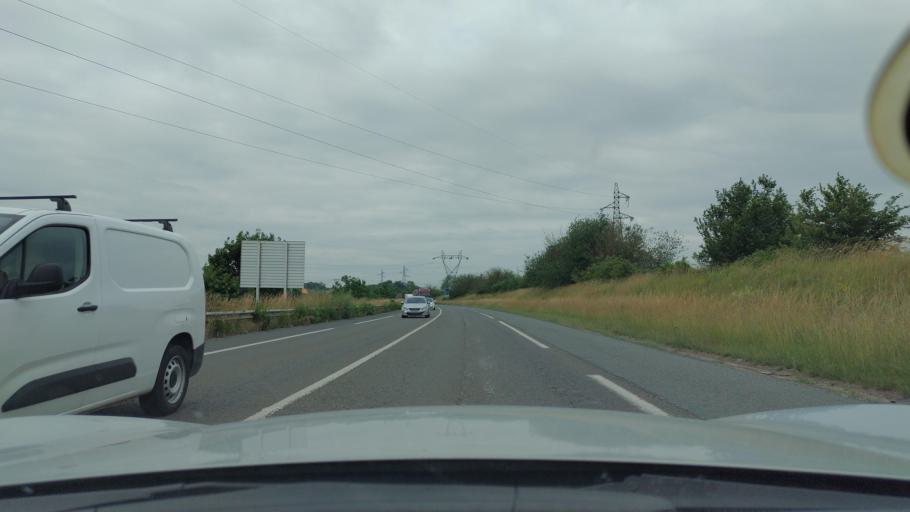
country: FR
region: Picardie
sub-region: Departement de l'Oise
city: Clairoix
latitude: 49.4379
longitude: 2.8399
